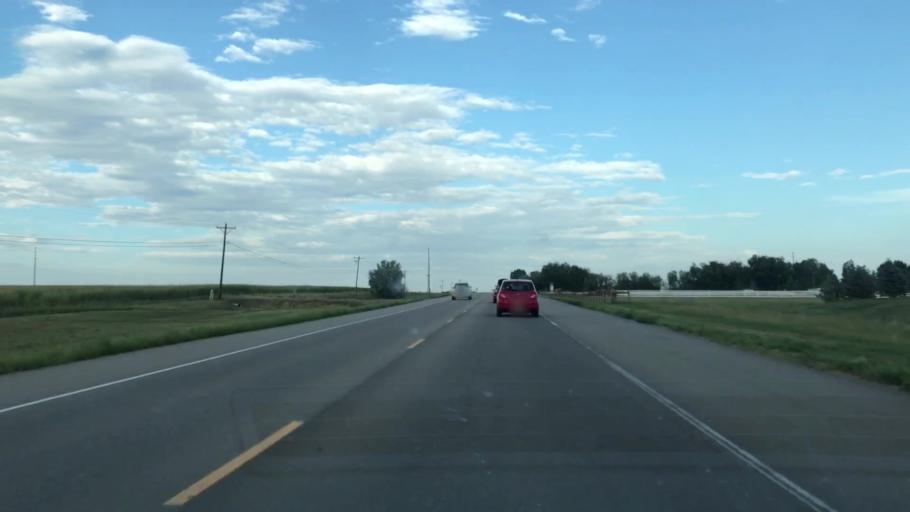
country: US
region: Colorado
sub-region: Weld County
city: Mead
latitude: 40.2037
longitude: -105.0445
